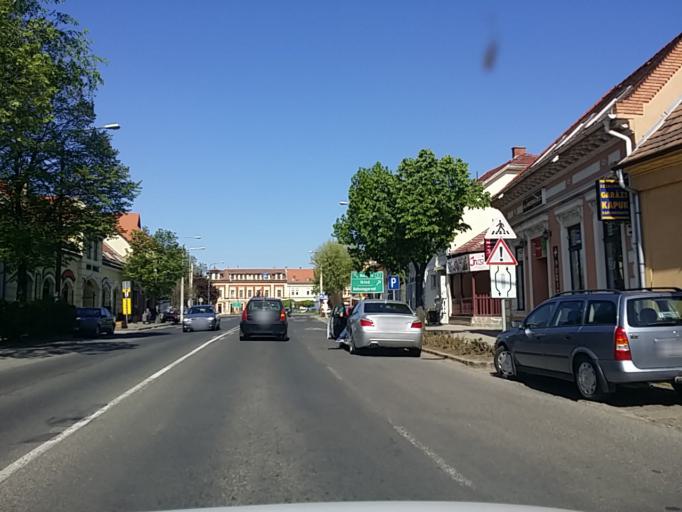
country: HU
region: Pest
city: Aszod
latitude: 47.6518
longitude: 19.4760
